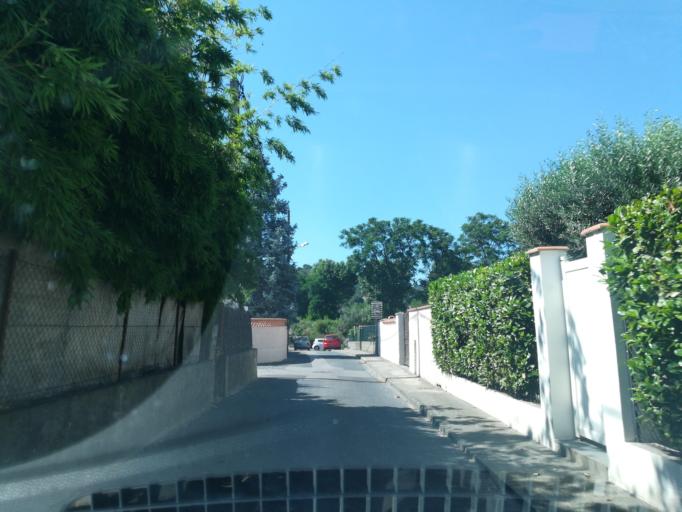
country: FR
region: Languedoc-Roussillon
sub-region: Departement des Pyrenees-Orientales
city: Ceret
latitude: 42.4936
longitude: 2.7419
